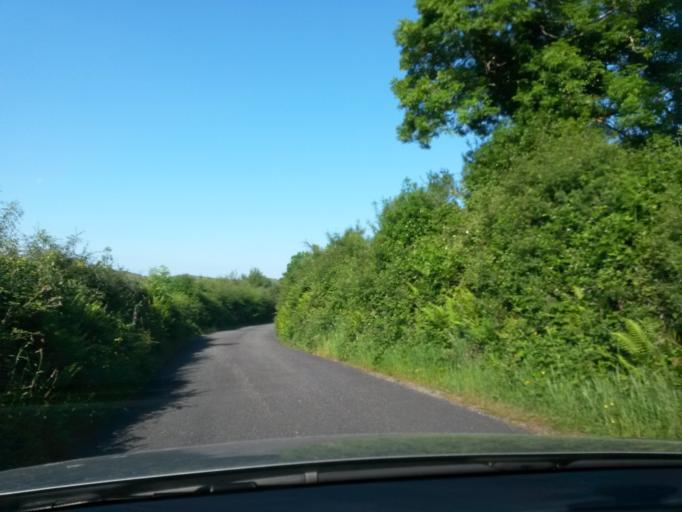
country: IE
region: Munster
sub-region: Ciarrai
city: Kenmare
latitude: 51.8028
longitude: -9.7598
